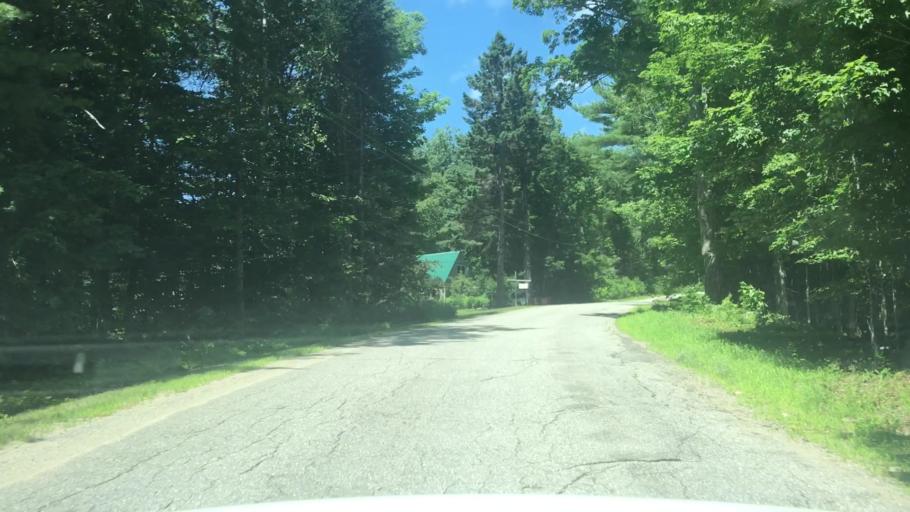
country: US
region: Maine
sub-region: Waldo County
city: Searsmont
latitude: 44.4529
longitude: -69.3131
